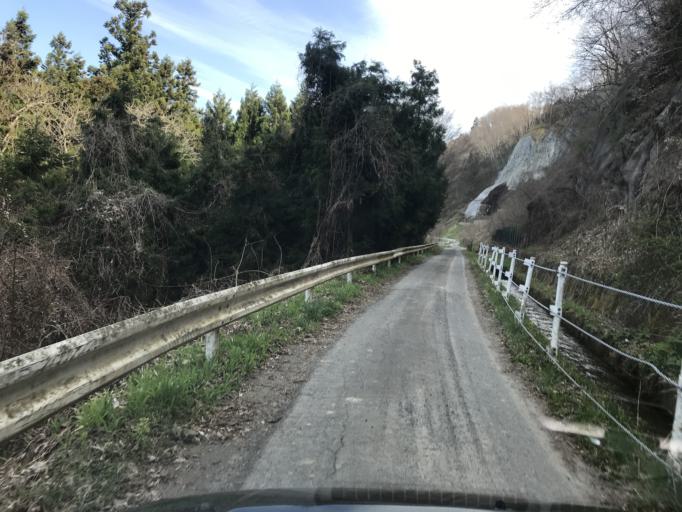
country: JP
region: Iwate
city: Ichinoseki
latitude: 38.9350
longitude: 141.0712
